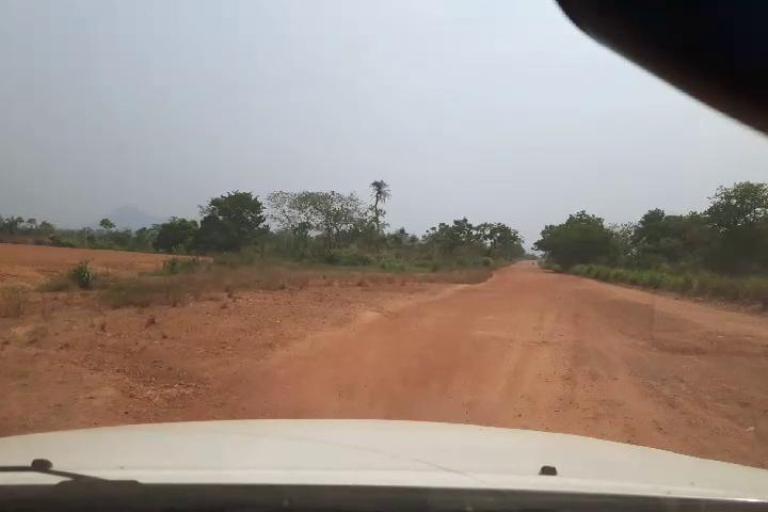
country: SL
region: Northern Province
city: Bumbuna
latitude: 9.0119
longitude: -11.7698
